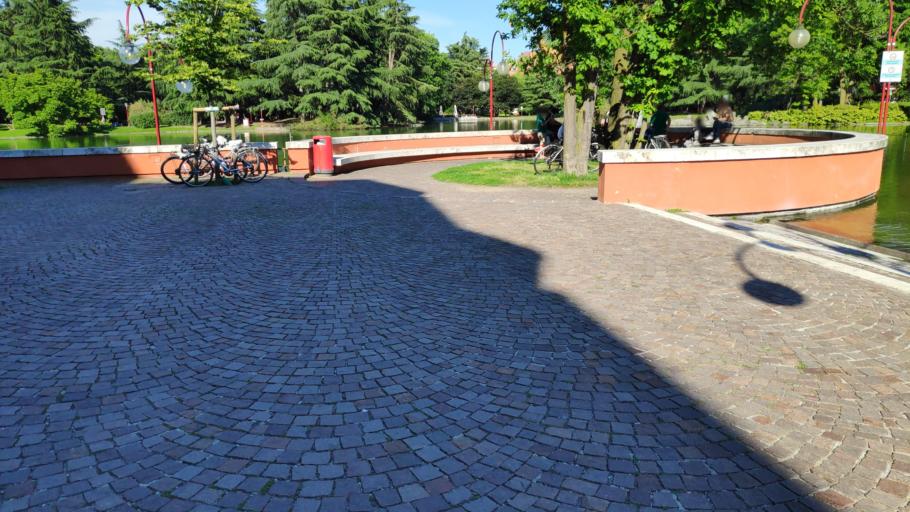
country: IT
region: Lombardy
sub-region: Citta metropolitana di Milano
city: Basiglio
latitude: 45.3592
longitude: 9.1581
